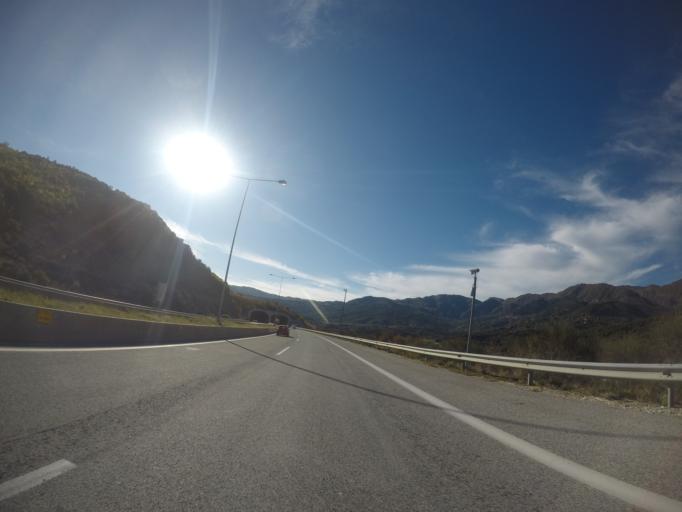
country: GR
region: Epirus
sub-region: Nomos Ioanninon
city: Metsovo
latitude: 39.7638
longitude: 21.1021
